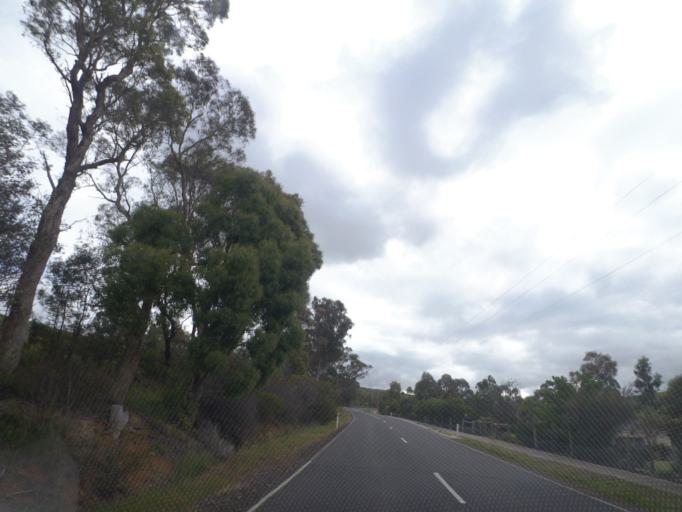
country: AU
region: Victoria
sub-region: Whittlesea
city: Whittlesea
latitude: -37.5255
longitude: 145.1101
